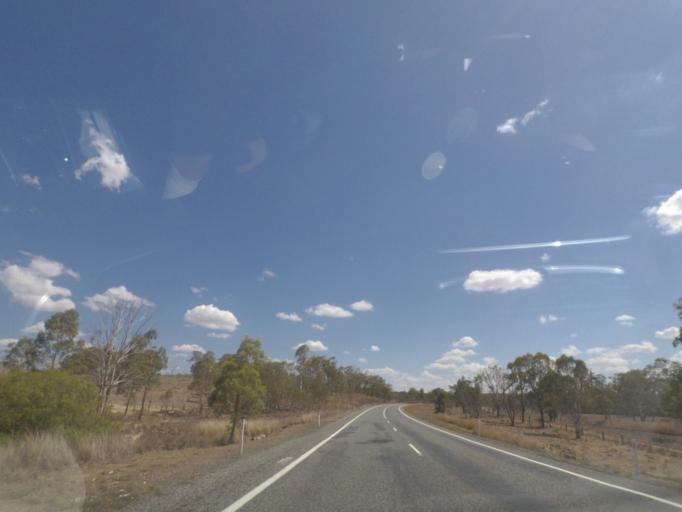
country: AU
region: Queensland
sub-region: Southern Downs
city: Warwick
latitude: -28.2127
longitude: 151.5641
